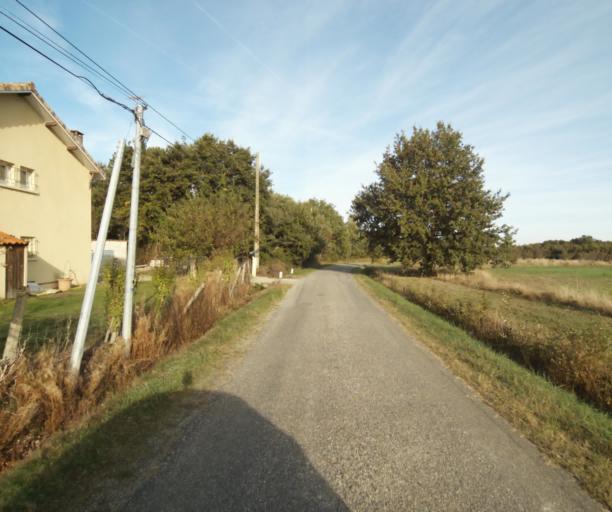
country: FR
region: Midi-Pyrenees
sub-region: Departement de la Haute-Garonne
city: Villemur-sur-Tarn
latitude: 43.9125
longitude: 1.5110
